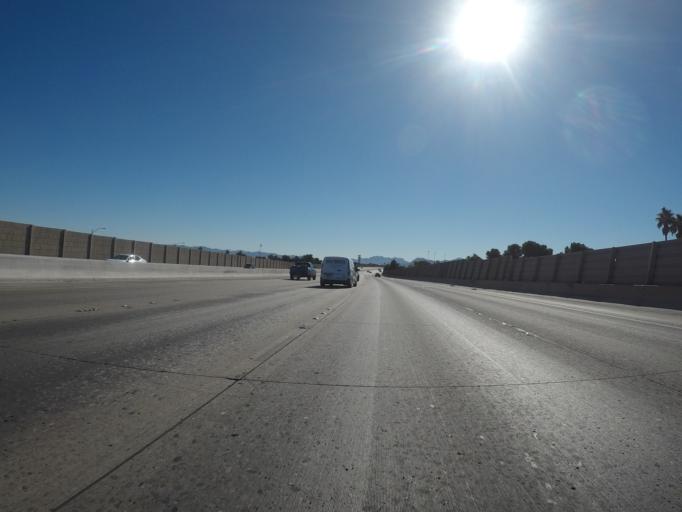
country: US
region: Nevada
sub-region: Clark County
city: Winchester
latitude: 36.1268
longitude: -115.0872
